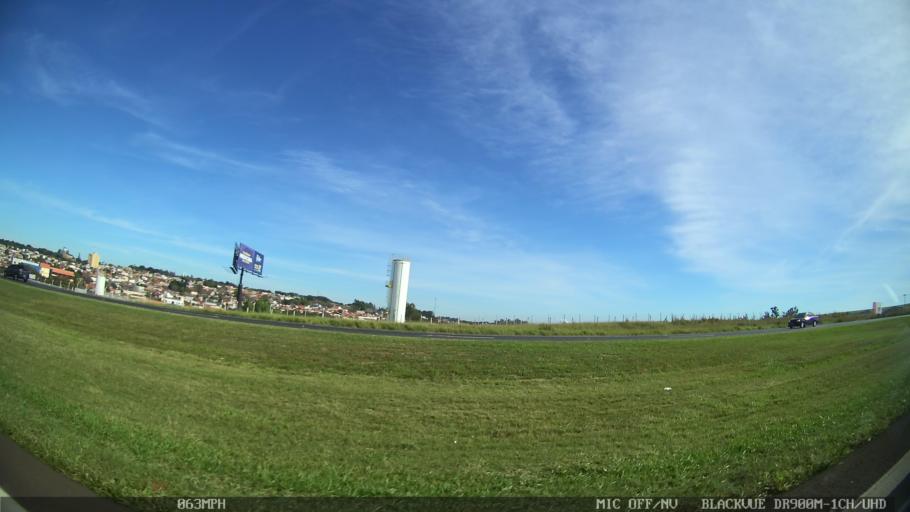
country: BR
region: Sao Paulo
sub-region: Araras
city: Araras
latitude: -22.3464
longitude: -47.3938
